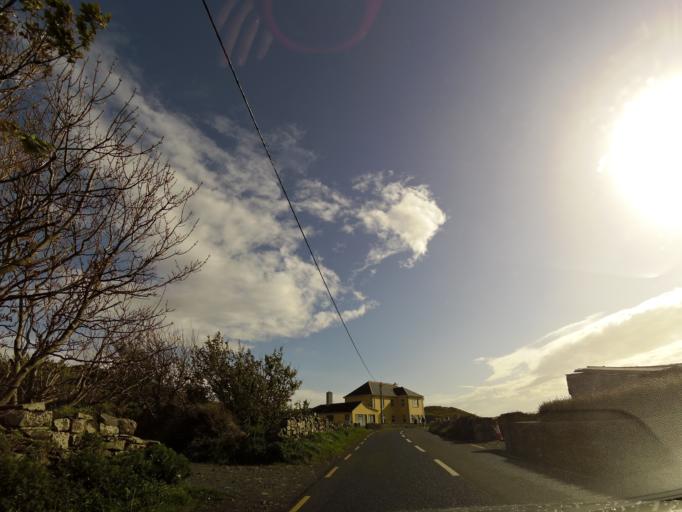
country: IE
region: Connaught
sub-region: County Galway
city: Bearna
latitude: 53.0179
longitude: -9.3721
